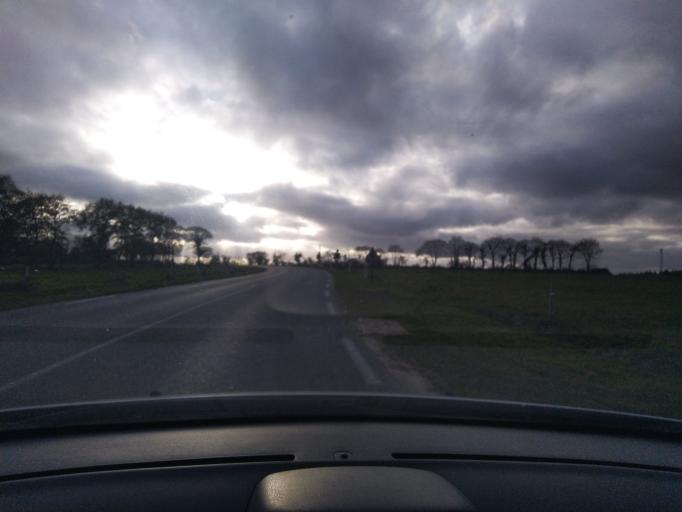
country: FR
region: Brittany
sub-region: Departement des Cotes-d'Armor
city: Plouaret
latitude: 48.6024
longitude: -3.4869
